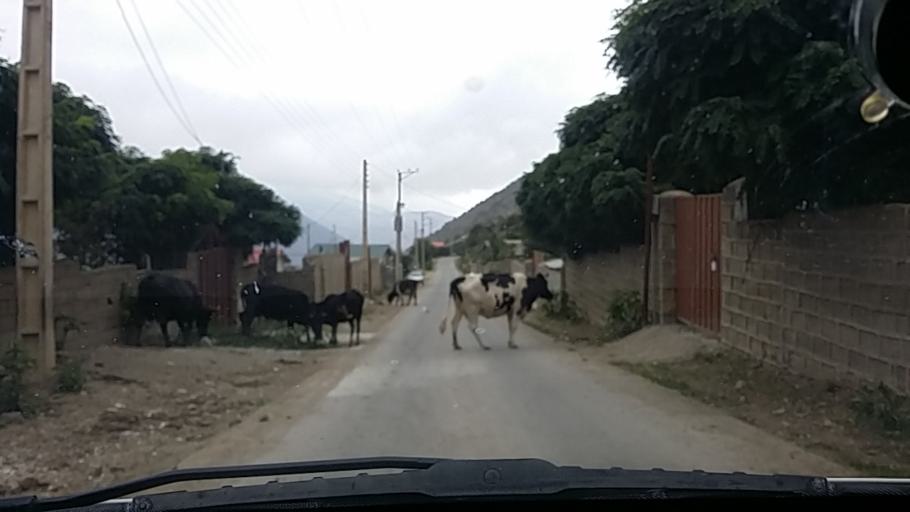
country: IR
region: Mazandaran
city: `Abbasabad
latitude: 36.4693
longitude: 51.1397
